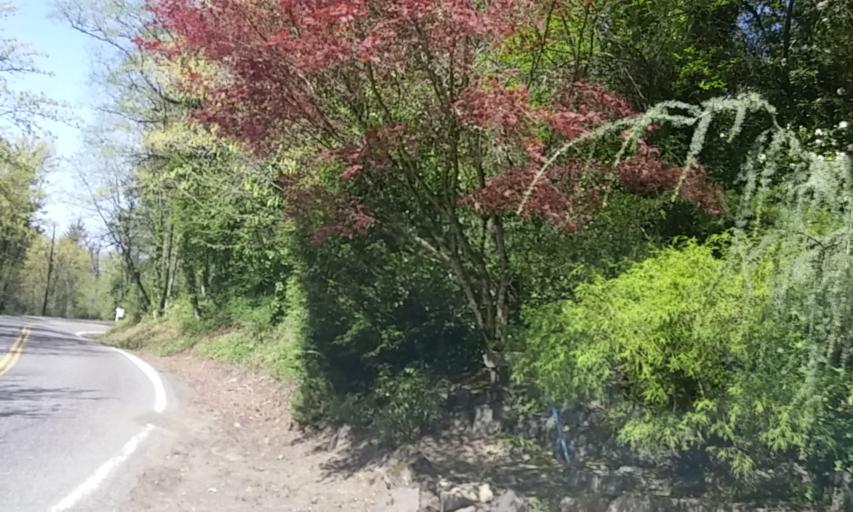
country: US
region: Oregon
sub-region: Washington County
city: West Haven-Sylvan
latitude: 45.5281
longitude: -122.7568
